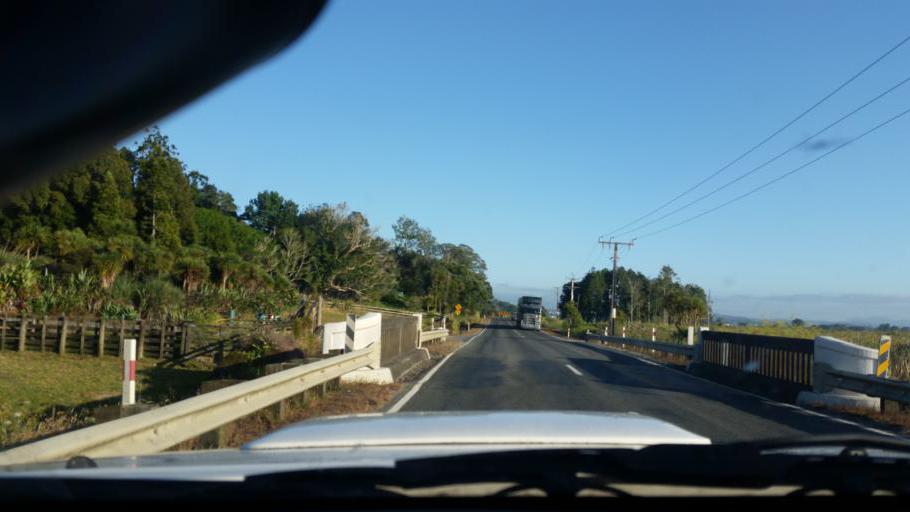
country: NZ
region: Northland
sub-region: Kaipara District
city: Dargaville
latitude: -35.9721
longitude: 173.8737
